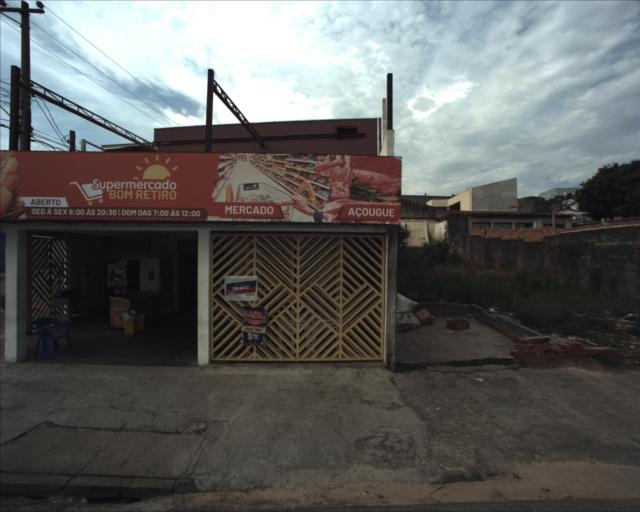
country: BR
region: Sao Paulo
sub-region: Sorocaba
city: Sorocaba
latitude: -23.4618
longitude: -47.4422
